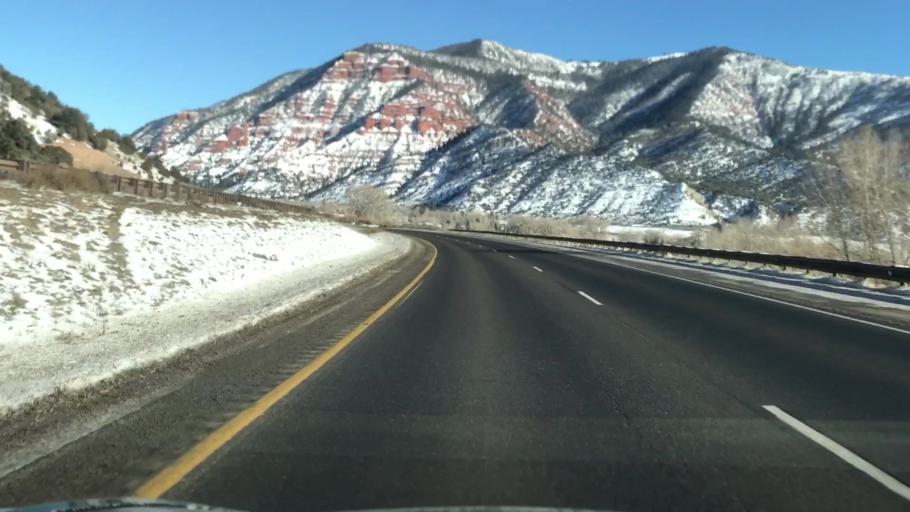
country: US
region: Colorado
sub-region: Eagle County
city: Eagle
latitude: 39.6800
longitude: -106.7676
